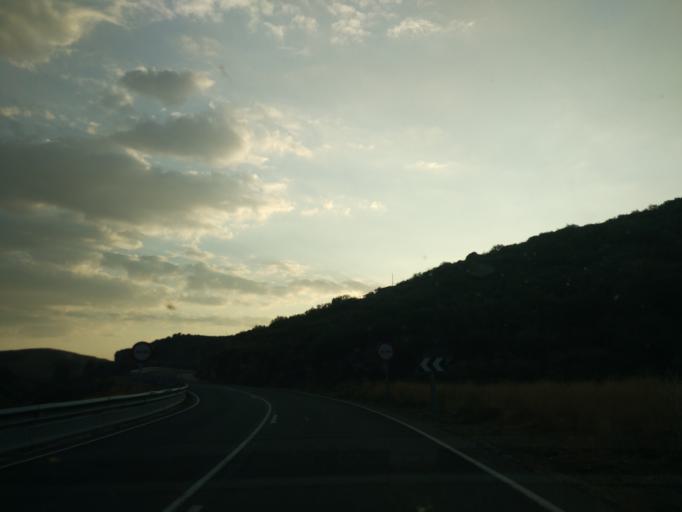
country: ES
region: Castille and Leon
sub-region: Provincia de Avila
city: San Martin del Pimpollar
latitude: 40.3721
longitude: -5.0333
